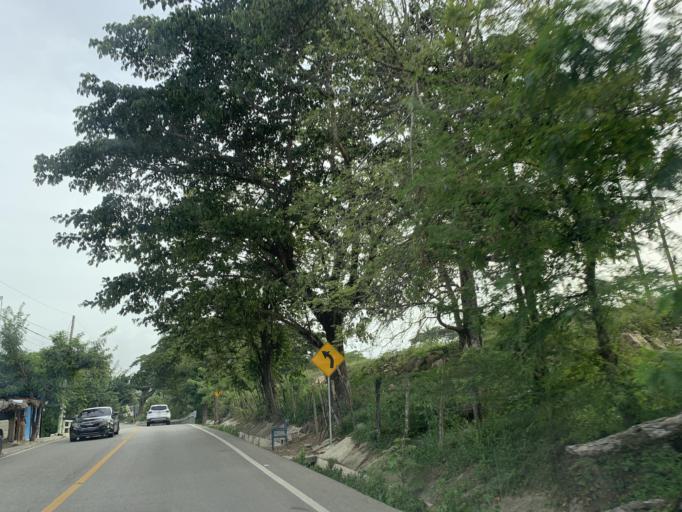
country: DO
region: Puerto Plata
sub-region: Puerto Plata
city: Puerto Plata
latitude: 19.7077
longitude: -70.6245
